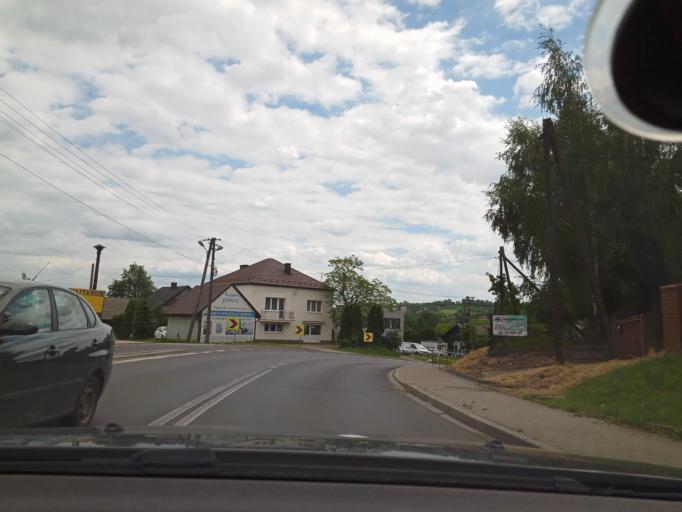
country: PL
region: Lesser Poland Voivodeship
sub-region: Powiat wielicki
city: Trabki
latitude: 49.9634
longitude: 20.1420
